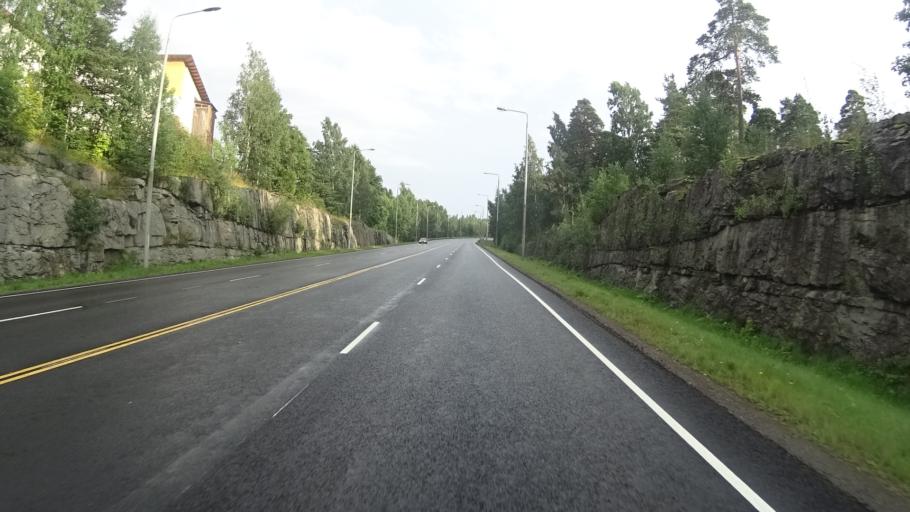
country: FI
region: Kymenlaakso
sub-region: Kotka-Hamina
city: Kotka
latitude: 60.4795
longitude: 26.9142
